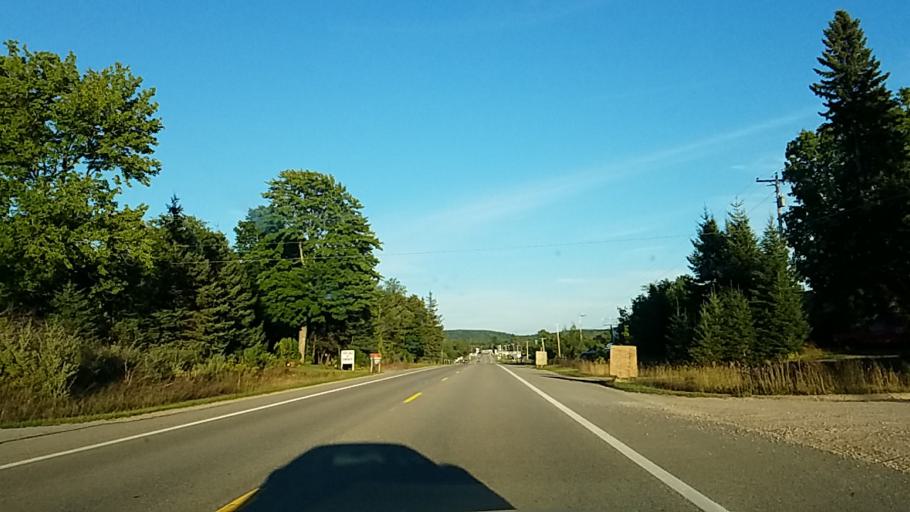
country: US
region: Michigan
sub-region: Alger County
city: Munising
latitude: 46.4395
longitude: -86.7157
